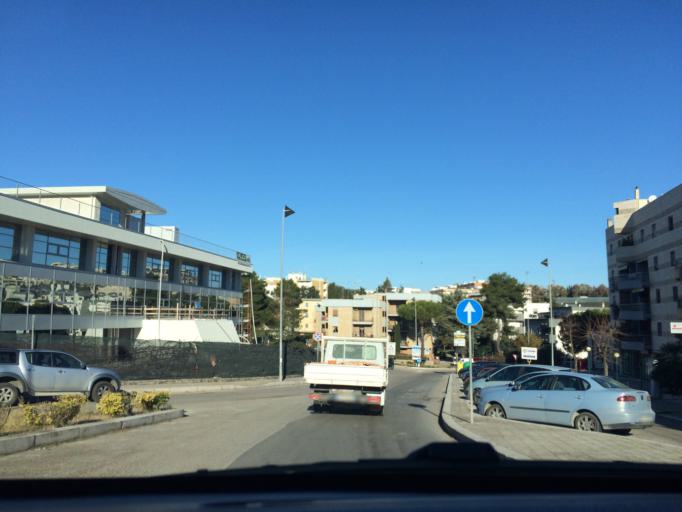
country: IT
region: Basilicate
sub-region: Provincia di Matera
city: Matera
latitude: 40.6628
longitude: 16.5971
